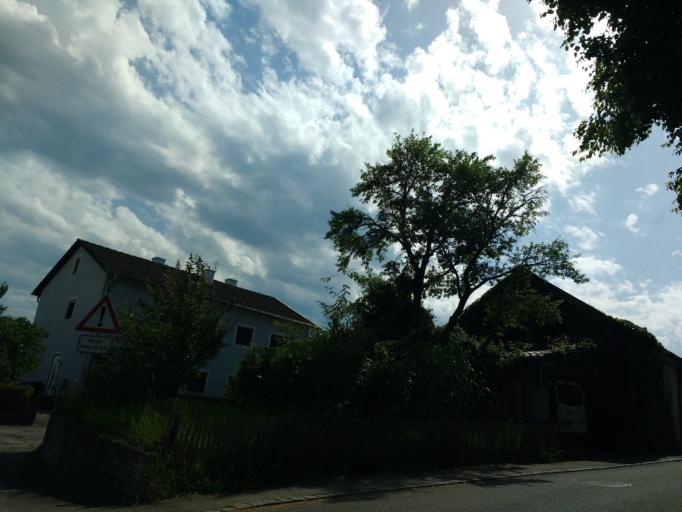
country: DE
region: Bavaria
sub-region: Upper Bavaria
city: Kienberg
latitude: 48.0344
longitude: 12.4649
